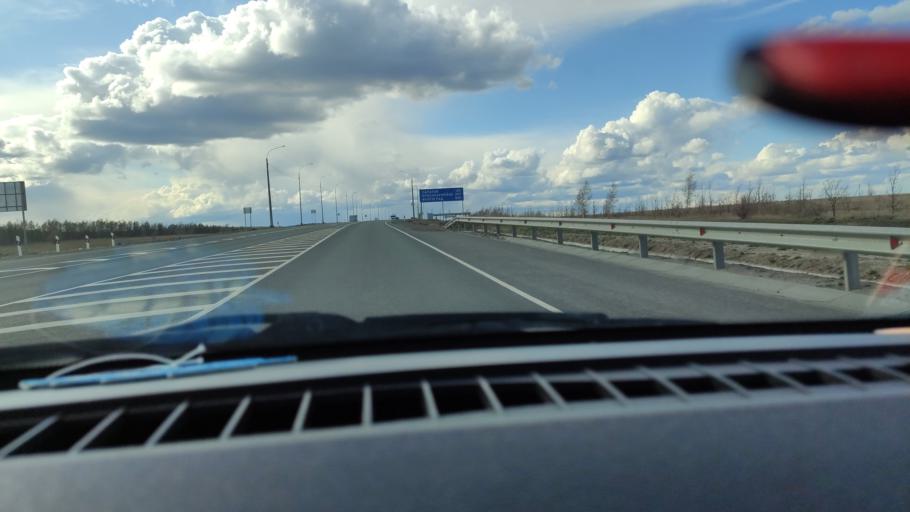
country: RU
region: Saratov
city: Shikhany
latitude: 52.1311
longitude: 47.2285
